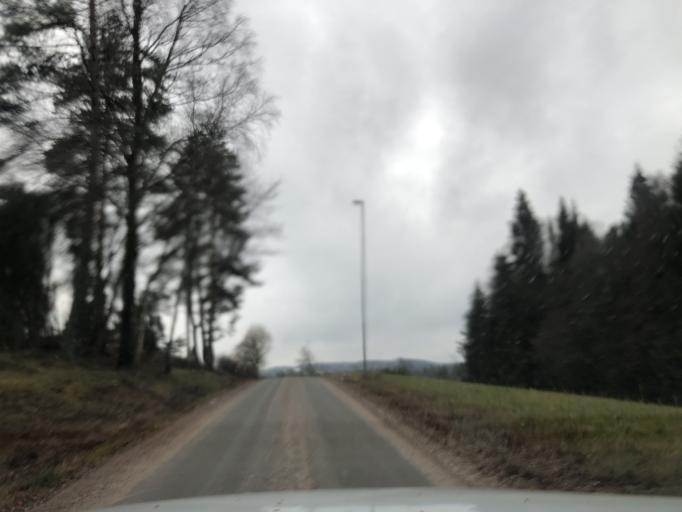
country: SE
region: Vaestra Goetaland
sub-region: Ulricehamns Kommun
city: Ulricehamn
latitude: 57.8680
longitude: 13.5559
